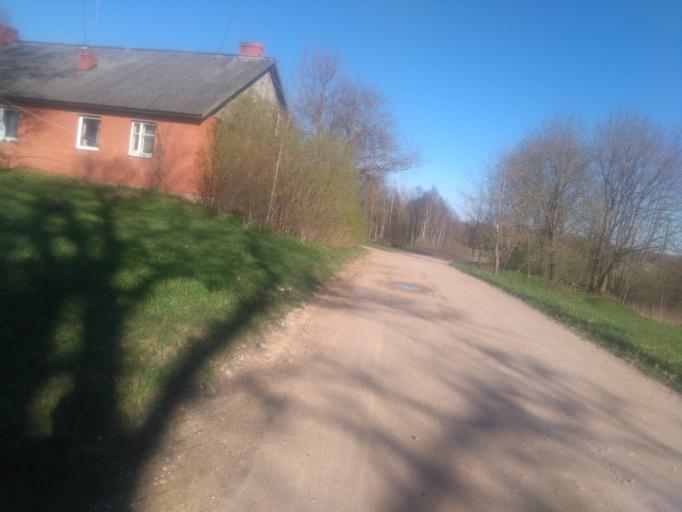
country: LV
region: Vecpiebalga
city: Vecpiebalga
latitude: 57.0190
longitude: 25.8507
